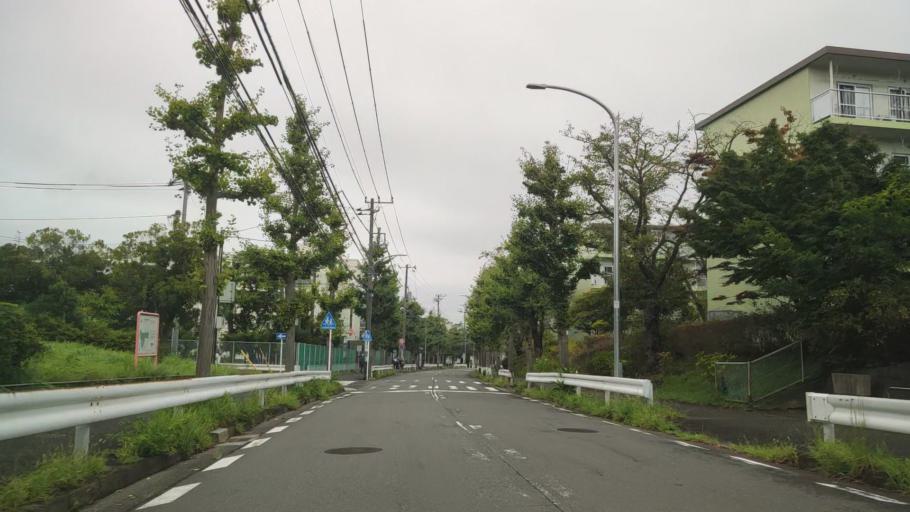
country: JP
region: Kanagawa
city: Zushi
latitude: 35.3681
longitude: 139.6092
